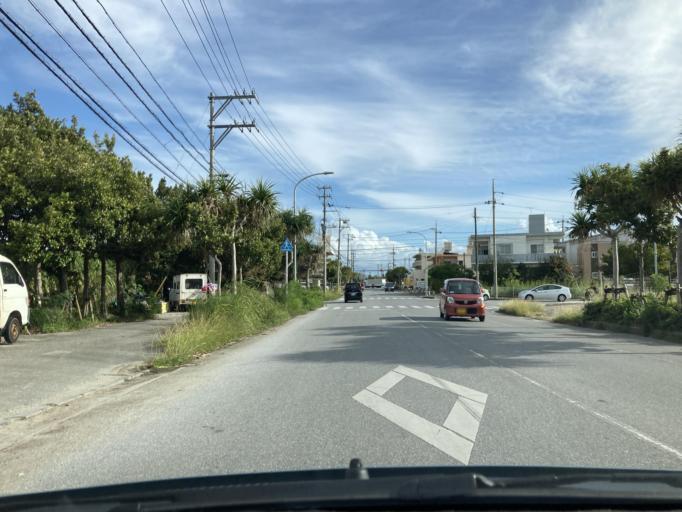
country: JP
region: Okinawa
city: Katsuren-haebaru
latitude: 26.3341
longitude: 127.8379
